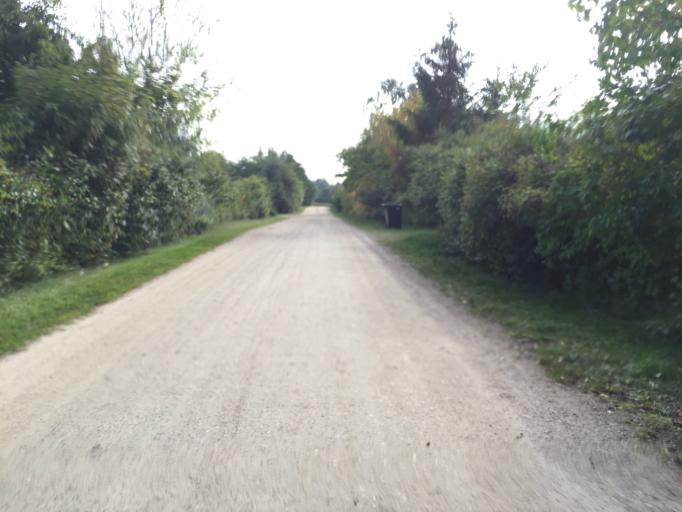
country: DK
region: Zealand
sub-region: Odsherred Kommune
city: Hojby
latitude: 55.8948
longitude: 11.5634
